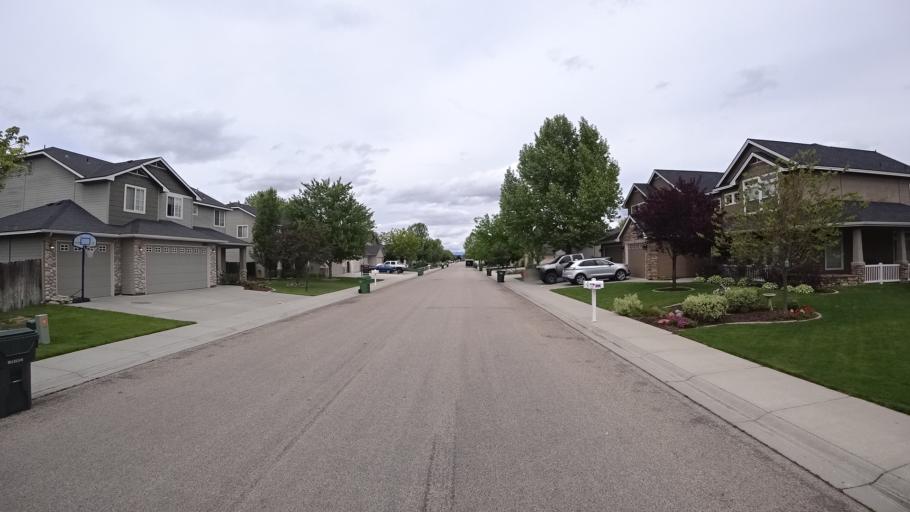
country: US
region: Idaho
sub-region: Ada County
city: Meridian
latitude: 43.6391
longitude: -116.4032
